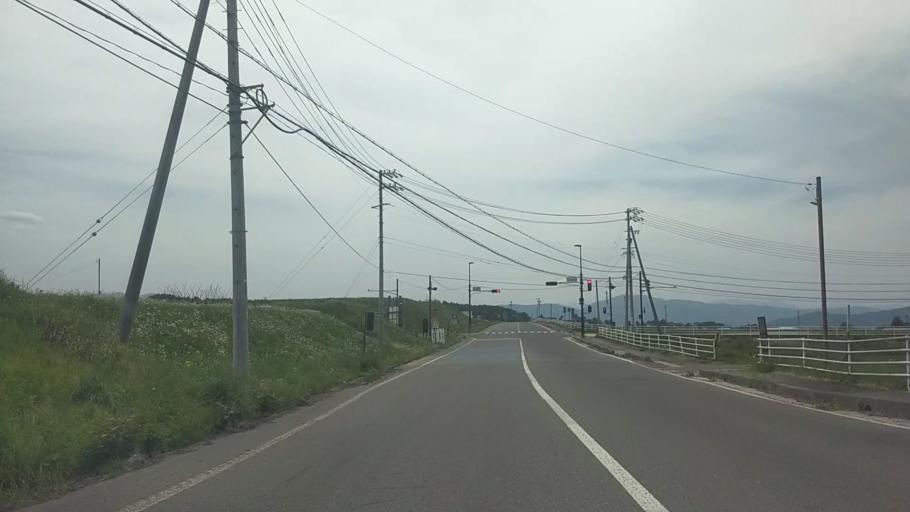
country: JP
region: Nagano
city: Chino
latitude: 36.0299
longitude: 138.2398
